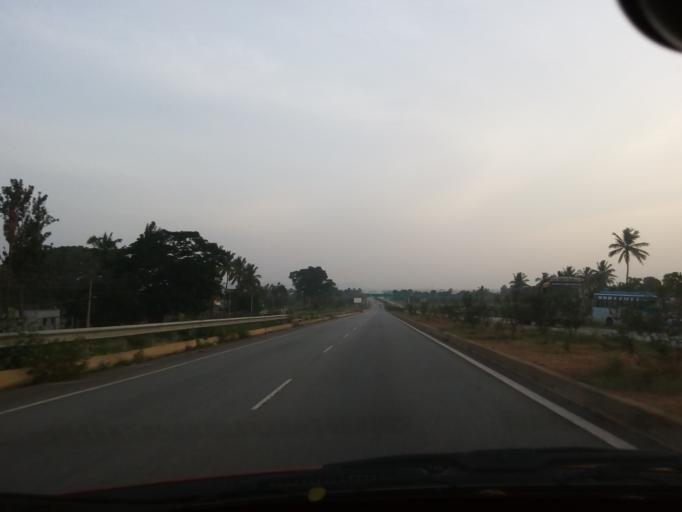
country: IN
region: Karnataka
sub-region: Bangalore Rural
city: Devanhalli
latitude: 13.2992
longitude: 77.7255
